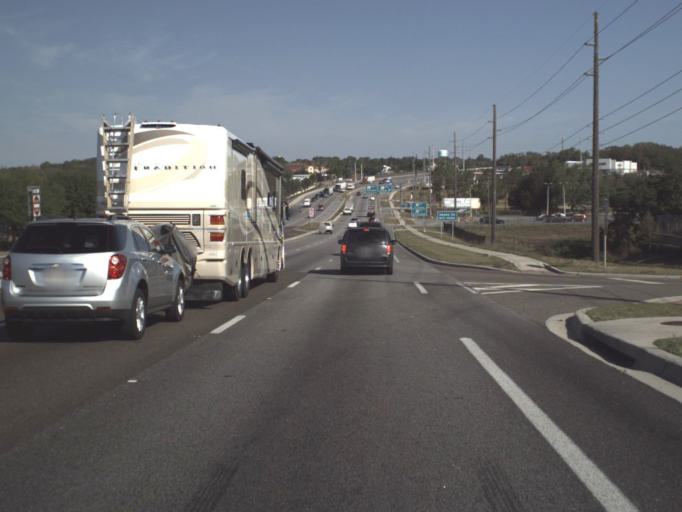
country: US
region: Florida
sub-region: Lake County
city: Clermont
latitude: 28.5383
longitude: -81.7383
